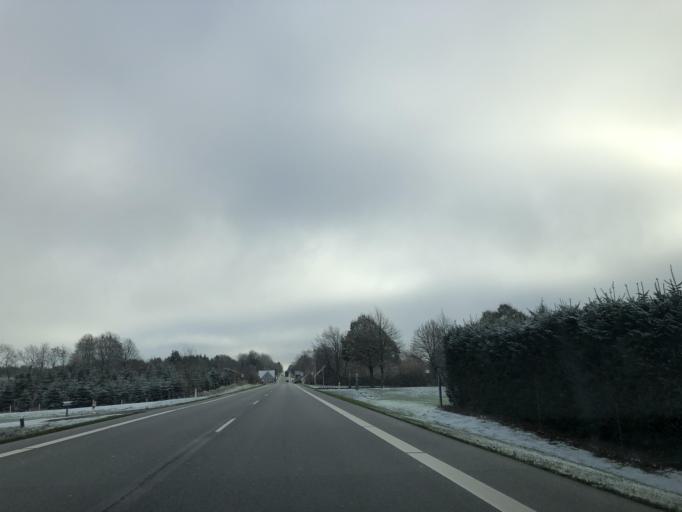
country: DK
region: Central Jutland
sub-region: Hedensted Kommune
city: Torring
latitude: 55.9489
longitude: 9.4394
